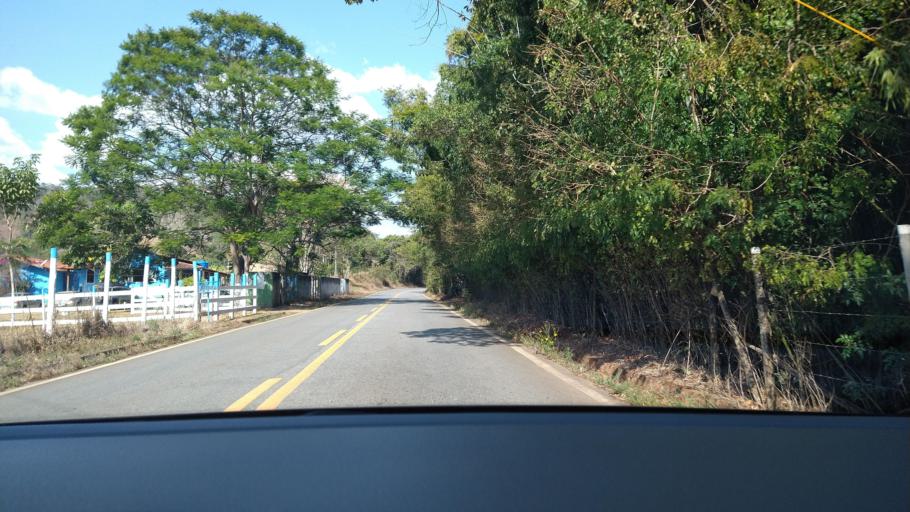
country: BR
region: Minas Gerais
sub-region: Rio Piracicaba
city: Rio Piracicaba
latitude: -19.9570
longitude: -43.1590
